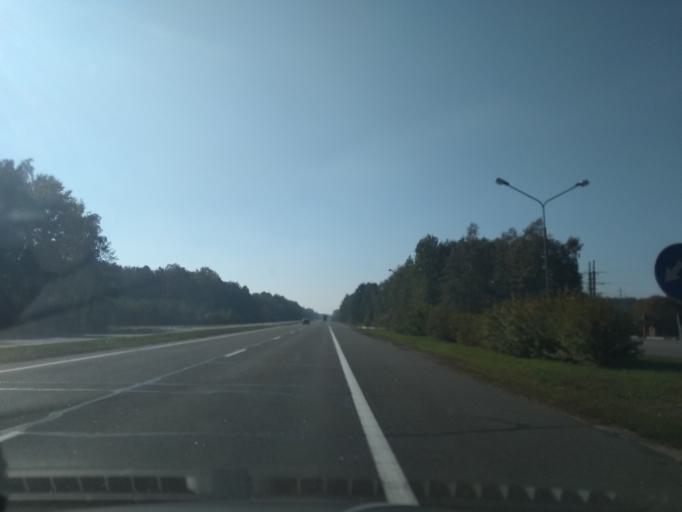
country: BY
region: Brest
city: Ivatsevichy
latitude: 52.6866
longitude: 25.3388
